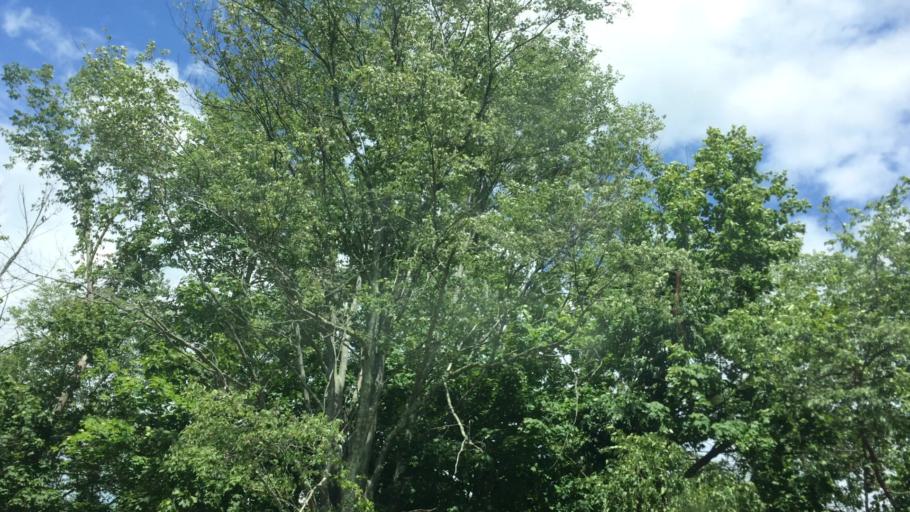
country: US
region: Massachusetts
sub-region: Middlesex County
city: Maynard
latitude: 42.4223
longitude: -71.4451
